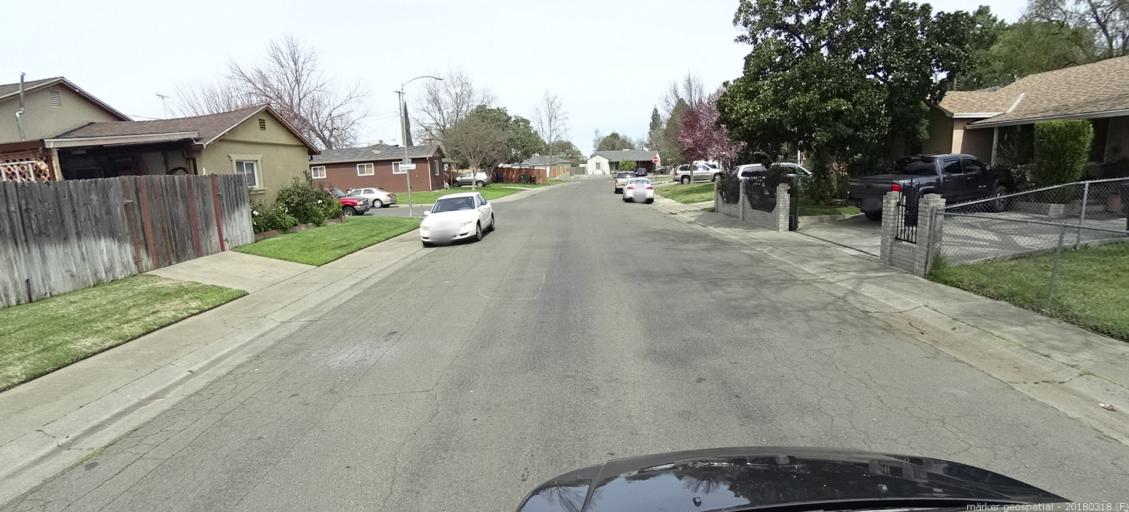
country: US
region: California
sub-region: Sacramento County
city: Parkway
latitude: 38.5189
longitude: -121.4512
